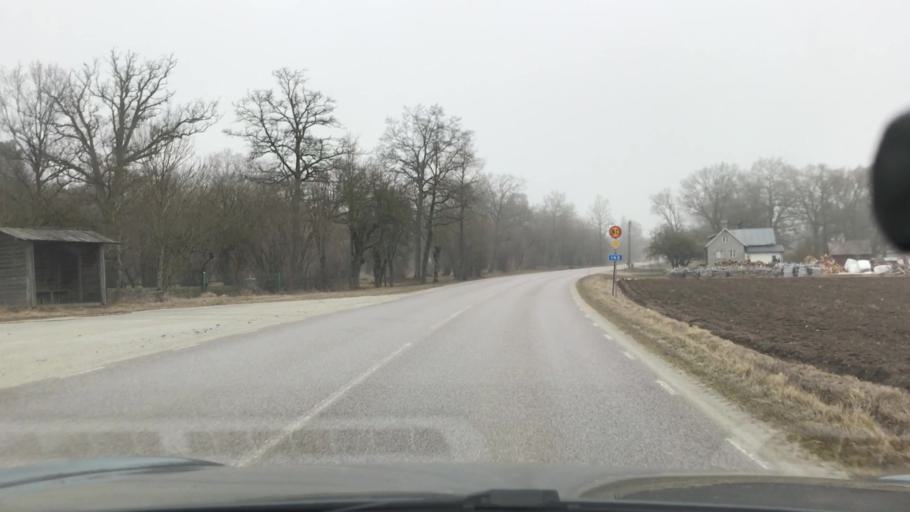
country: SE
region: Gotland
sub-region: Gotland
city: Hemse
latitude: 57.3095
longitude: 18.3800
